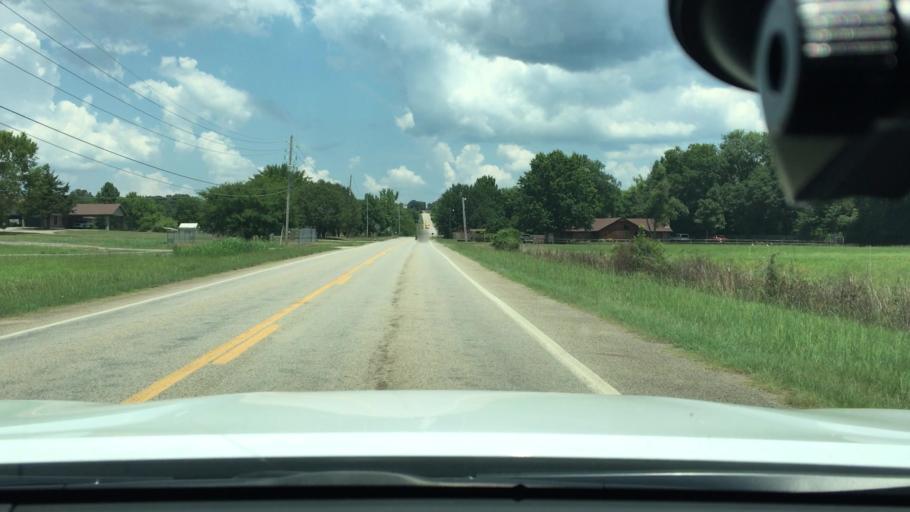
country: US
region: Arkansas
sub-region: Logan County
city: Booneville
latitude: 35.1486
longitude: -93.8772
